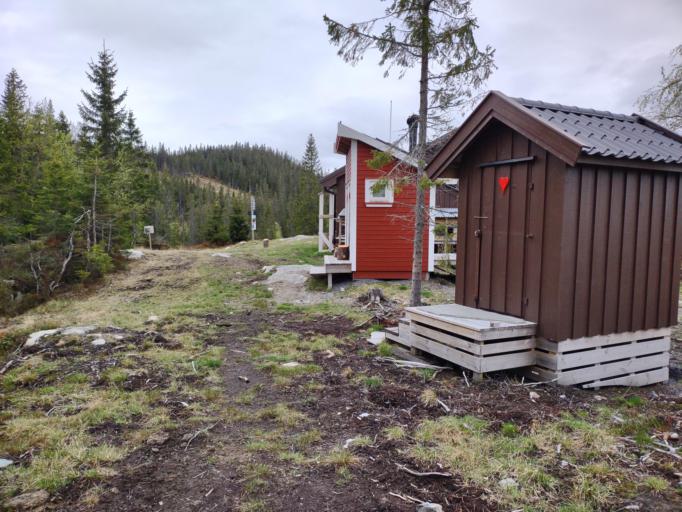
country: NO
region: Oppland
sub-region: Gran
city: Jaren
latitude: 60.4316
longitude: 10.6814
